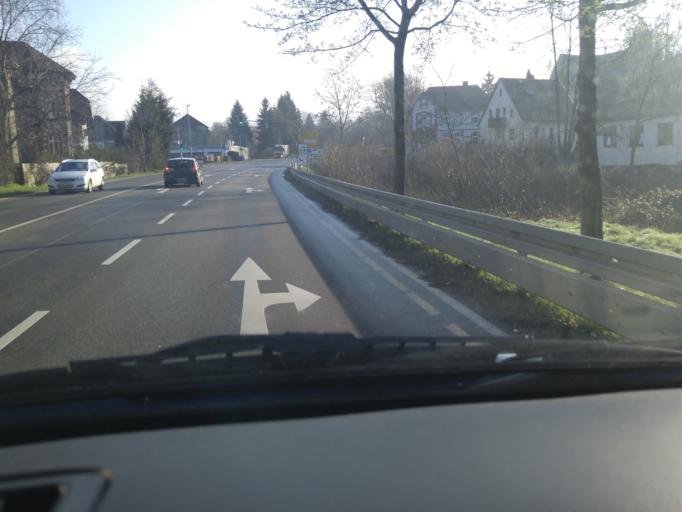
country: DE
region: Hesse
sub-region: Regierungsbezirk Giessen
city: Schotten
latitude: 50.4991
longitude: 9.1205
